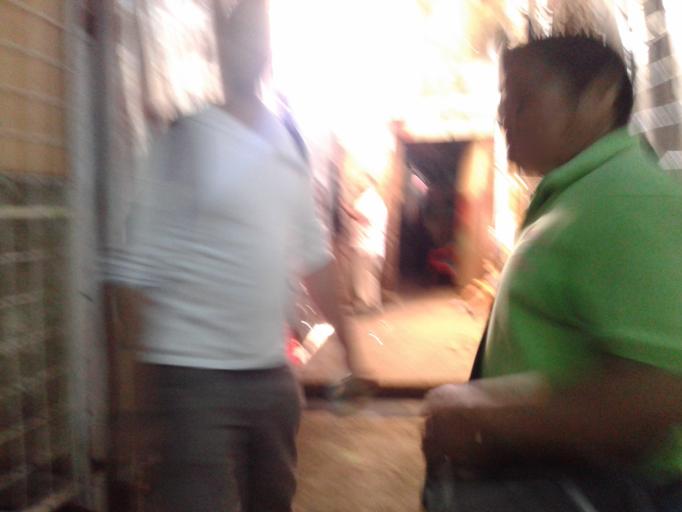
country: NI
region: Managua
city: Managua
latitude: 12.1482
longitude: -86.2611
